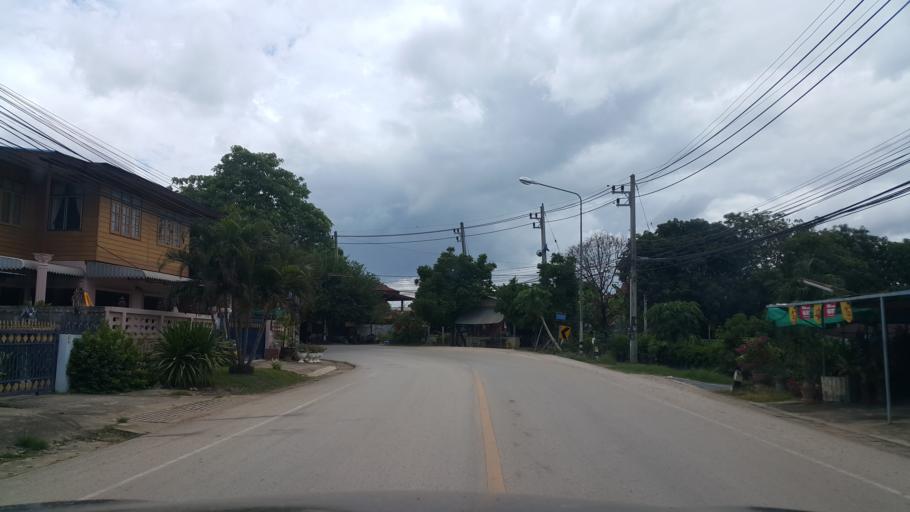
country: TH
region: Sukhothai
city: Sukhothai
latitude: 17.0046
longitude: 99.8330
